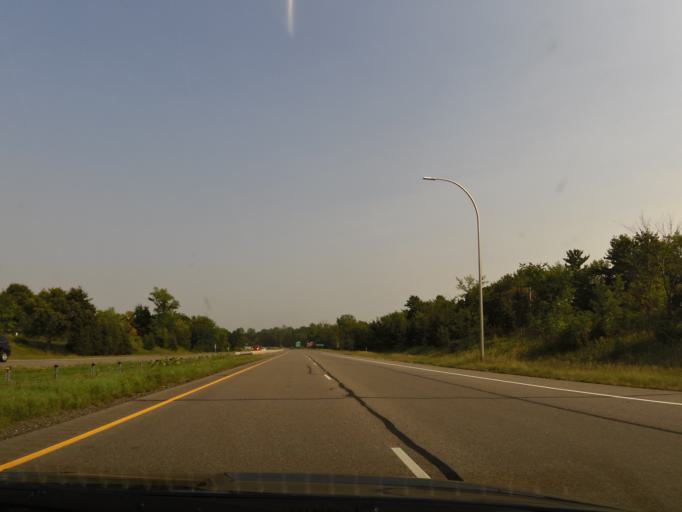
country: US
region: Minnesota
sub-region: Stearns County
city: Avon
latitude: 45.6028
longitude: -94.4777
